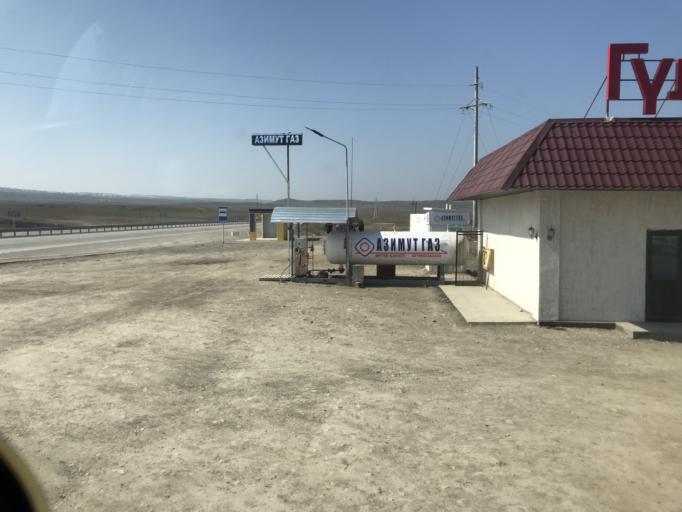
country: KZ
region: Zhambyl
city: Georgiyevka
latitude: 43.4125
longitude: 75.0621
